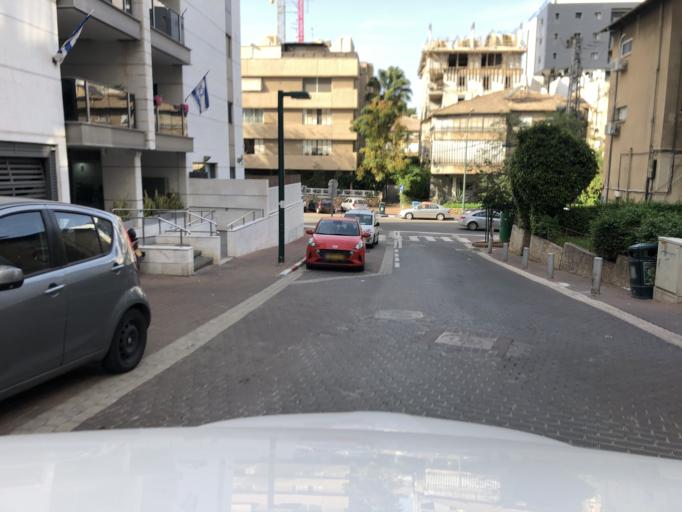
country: IL
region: Tel Aviv
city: Bene Beraq
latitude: 32.0775
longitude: 34.8257
